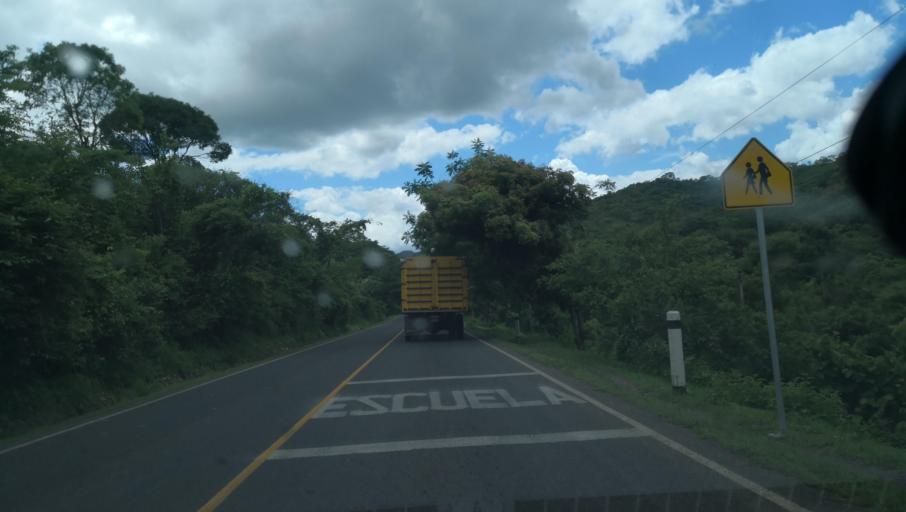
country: NI
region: Madriz
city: Yalaguina
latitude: 13.4614
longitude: -86.4676
